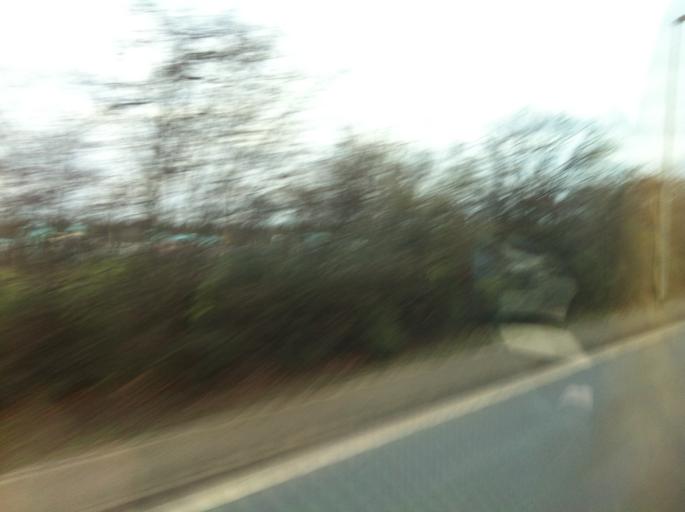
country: DE
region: Rheinland-Pfalz
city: Bad Kreuznach
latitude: 49.8559
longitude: 7.8793
